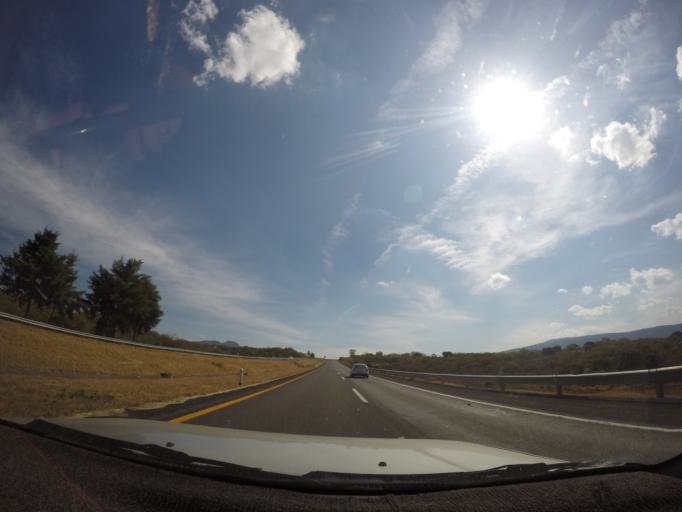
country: MX
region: Michoacan
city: Panindicuaro de la Reforma
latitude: 19.9989
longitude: -101.8748
